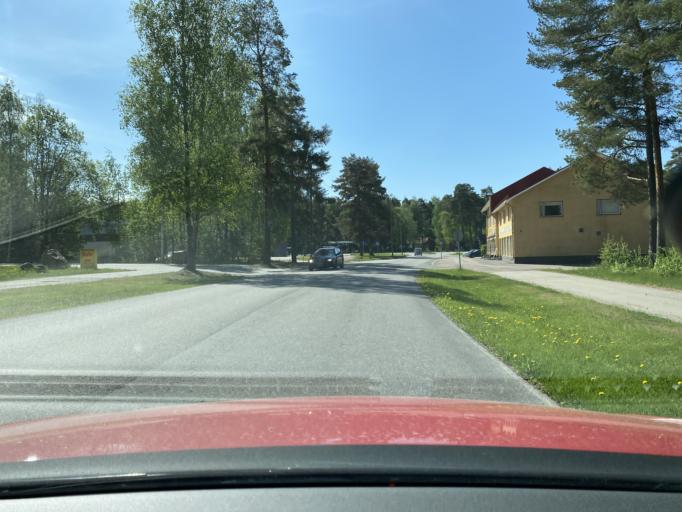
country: FI
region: Satakunta
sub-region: Rauma
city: Eura
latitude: 61.1172
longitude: 22.1611
